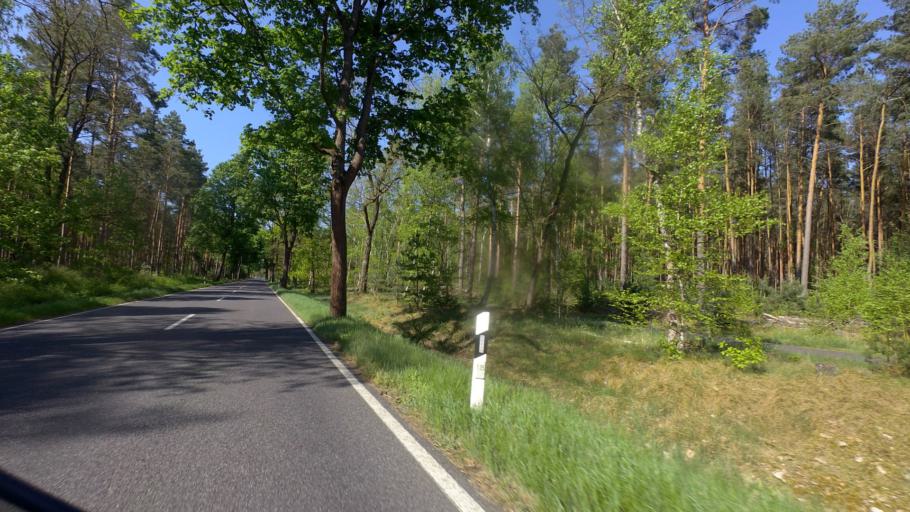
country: DE
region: Brandenburg
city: Halbe
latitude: 52.1457
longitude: 13.7465
